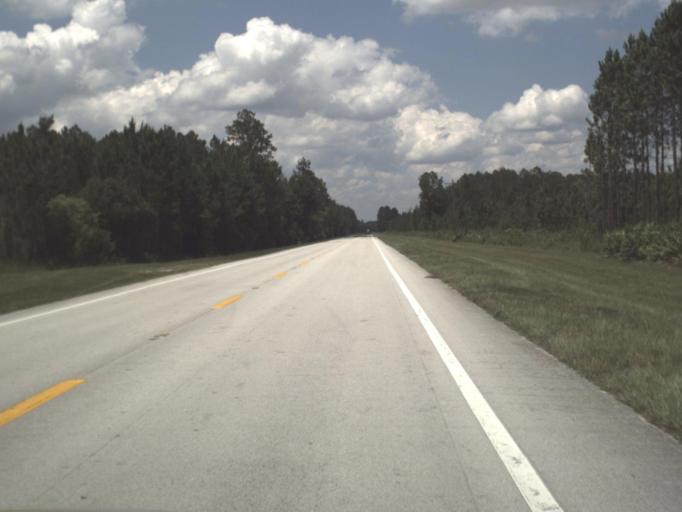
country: US
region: Florida
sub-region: Baker County
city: Macclenny
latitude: 30.2065
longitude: -82.1556
